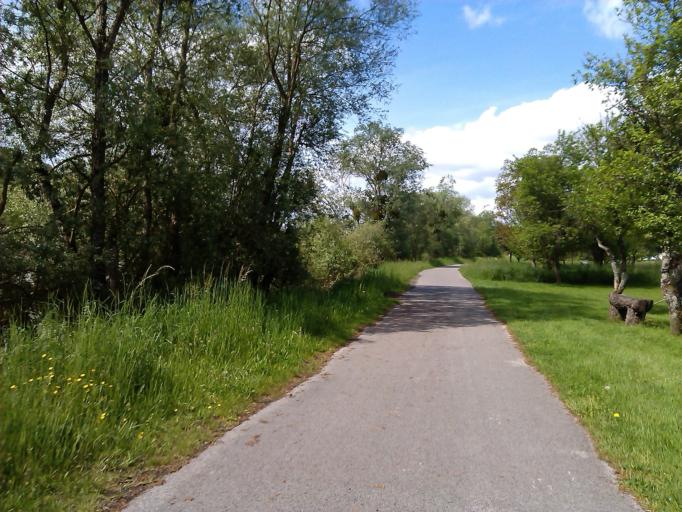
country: FR
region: Franche-Comte
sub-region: Departement du Doubs
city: Novillars
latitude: 47.2851
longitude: 6.1456
